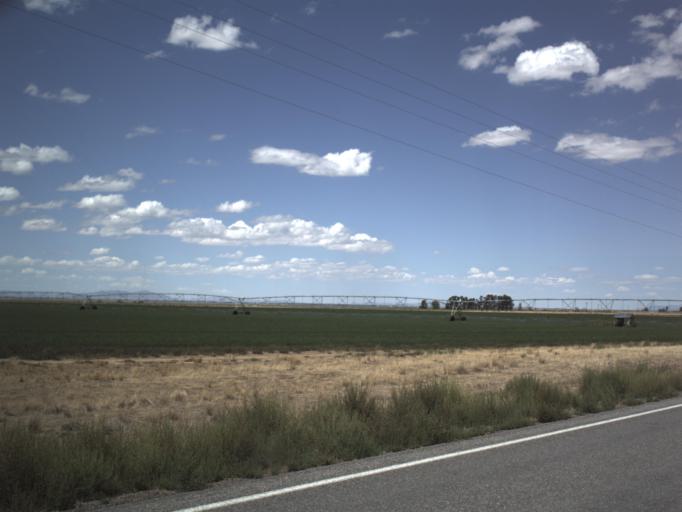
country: US
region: Utah
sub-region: Millard County
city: Delta
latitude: 39.1888
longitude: -112.4100
